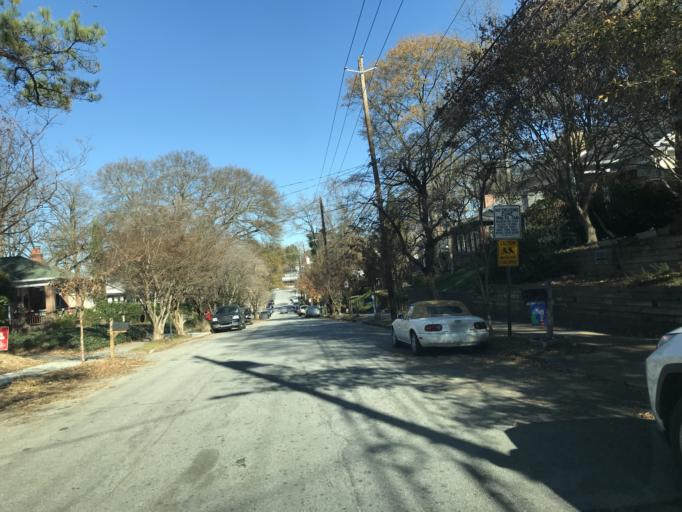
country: US
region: Georgia
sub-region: DeKalb County
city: Druid Hills
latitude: 33.7716
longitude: -84.3623
